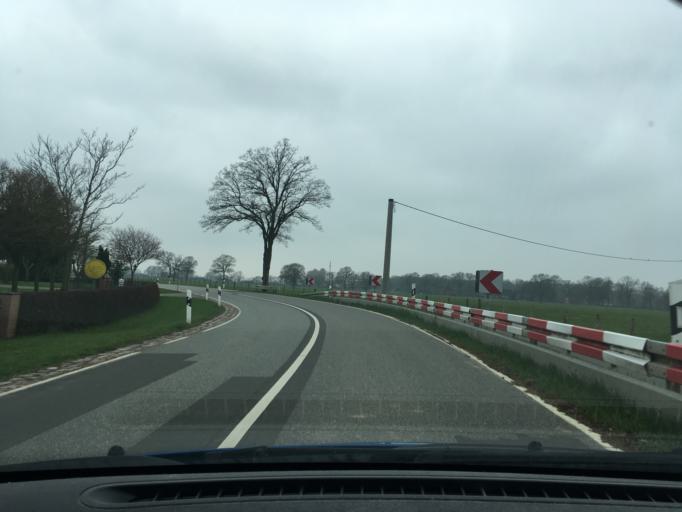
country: DE
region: Lower Saxony
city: Bleckede
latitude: 53.3250
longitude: 10.8208
